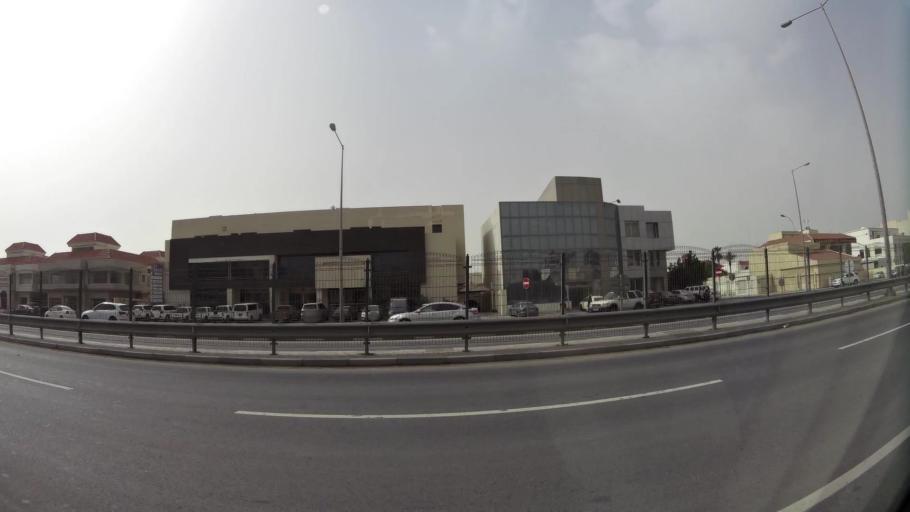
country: QA
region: Baladiyat ad Dawhah
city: Doha
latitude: 25.2630
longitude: 51.5301
